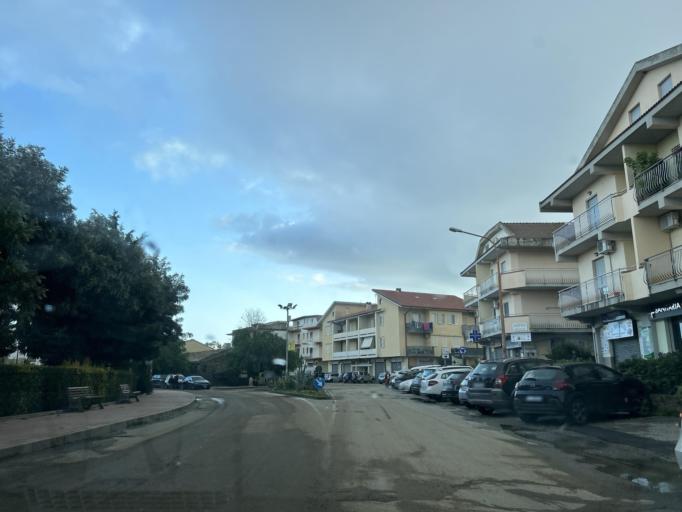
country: IT
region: Calabria
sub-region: Provincia di Catanzaro
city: Squillace Lido
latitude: 38.7782
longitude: 16.5693
